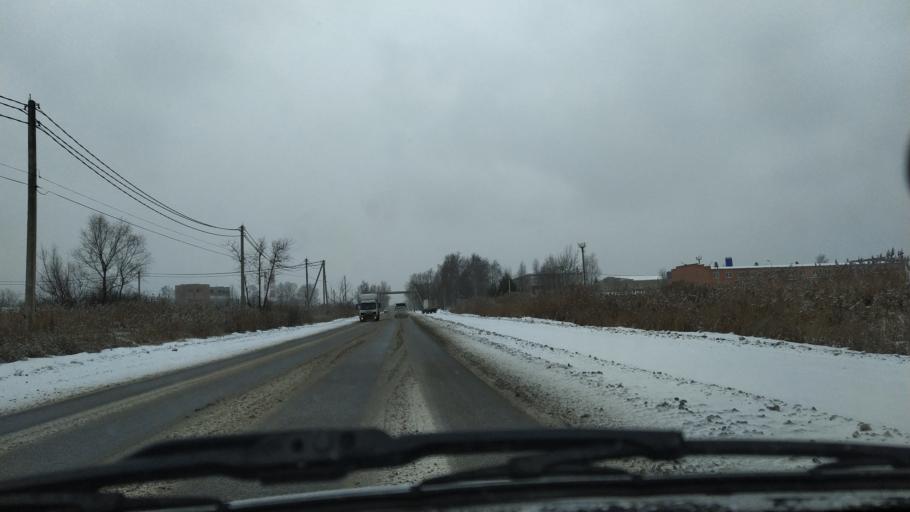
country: RU
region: Moskovskaya
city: Lopatinskiy
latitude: 55.3495
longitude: 38.7390
